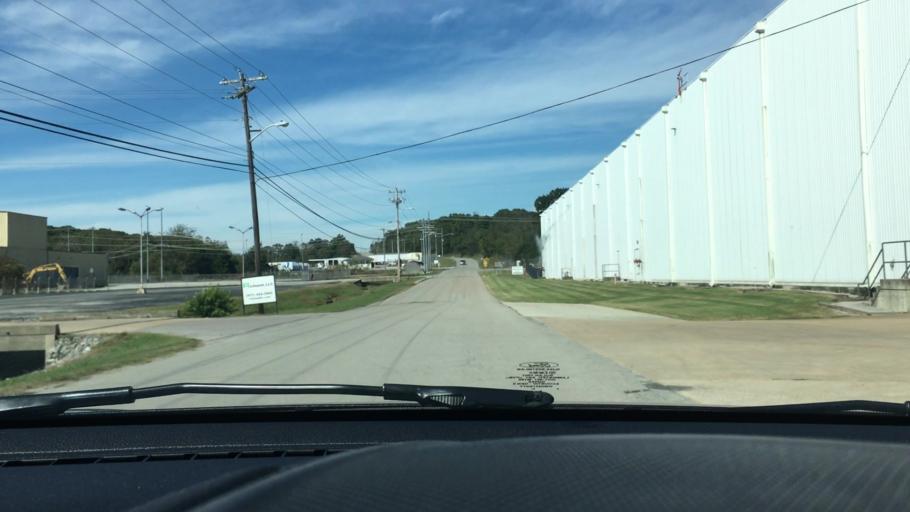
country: US
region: Tennessee
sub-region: Giles County
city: Pulaski
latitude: 35.2155
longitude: -87.0613
